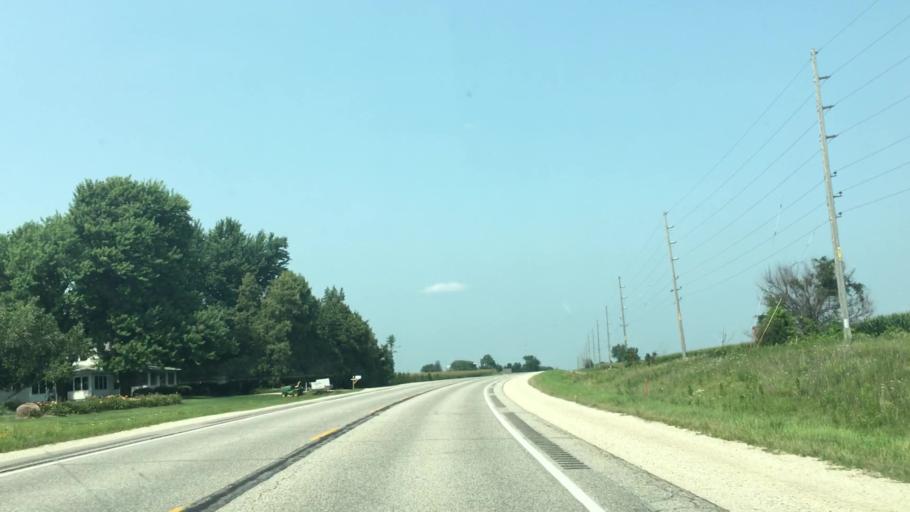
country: US
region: Iowa
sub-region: Fayette County
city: West Union
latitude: 42.9114
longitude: -91.8143
